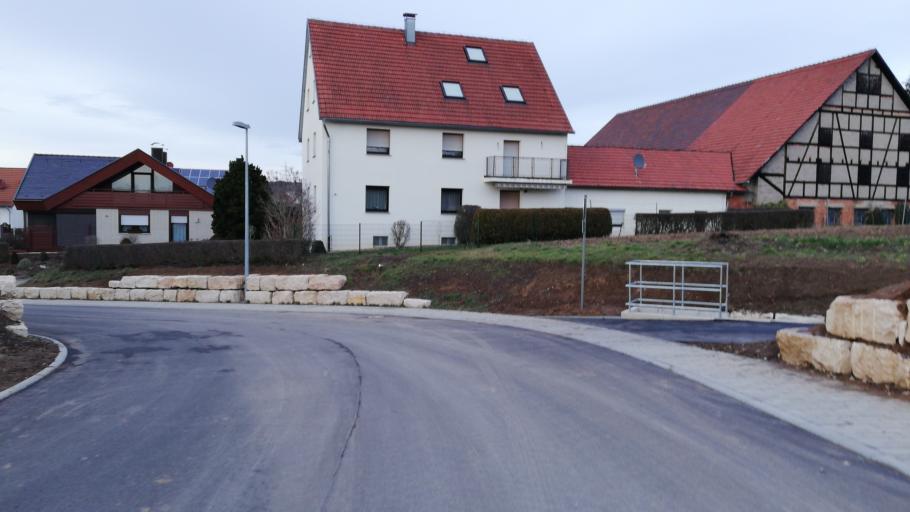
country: DE
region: Baden-Wuerttemberg
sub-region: Regierungsbezirk Stuttgart
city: Schwaikheim
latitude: 48.8890
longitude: 9.3203
